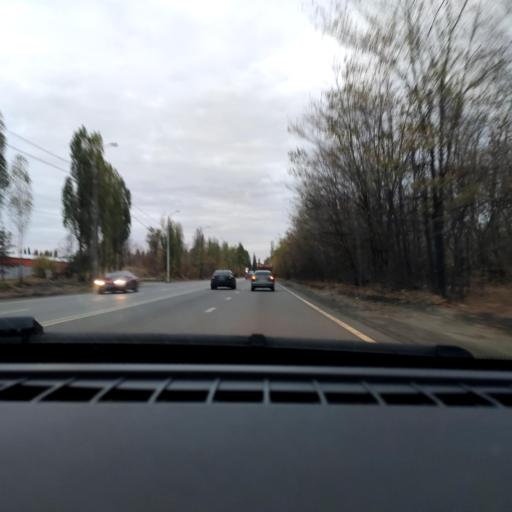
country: RU
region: Voronezj
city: Maslovka
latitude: 51.6060
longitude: 39.2550
